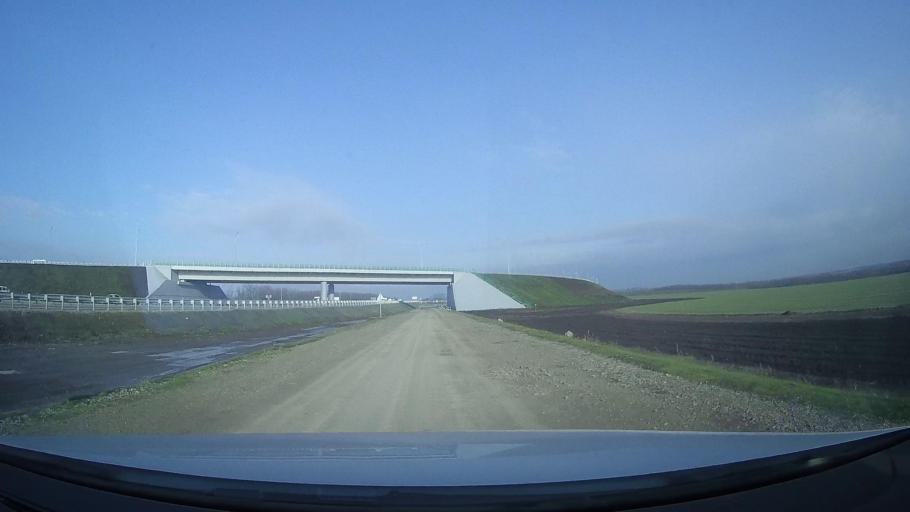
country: RU
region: Rostov
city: Grushevskaya
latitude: 47.5020
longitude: 39.9711
